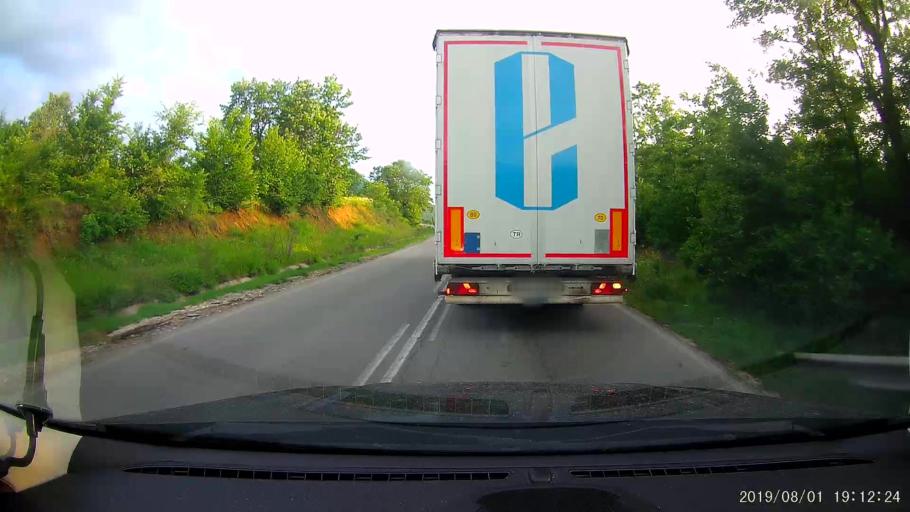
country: BG
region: Shumen
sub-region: Obshtina Smyadovo
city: Smyadovo
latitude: 42.9647
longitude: 26.9506
